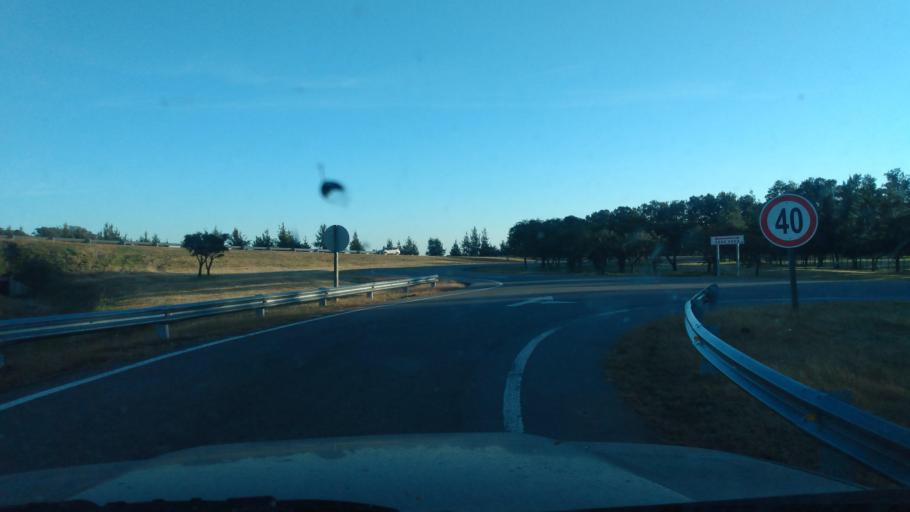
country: AR
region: Buenos Aires
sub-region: Partido de Lujan
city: Lujan
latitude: -34.5381
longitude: -59.2552
